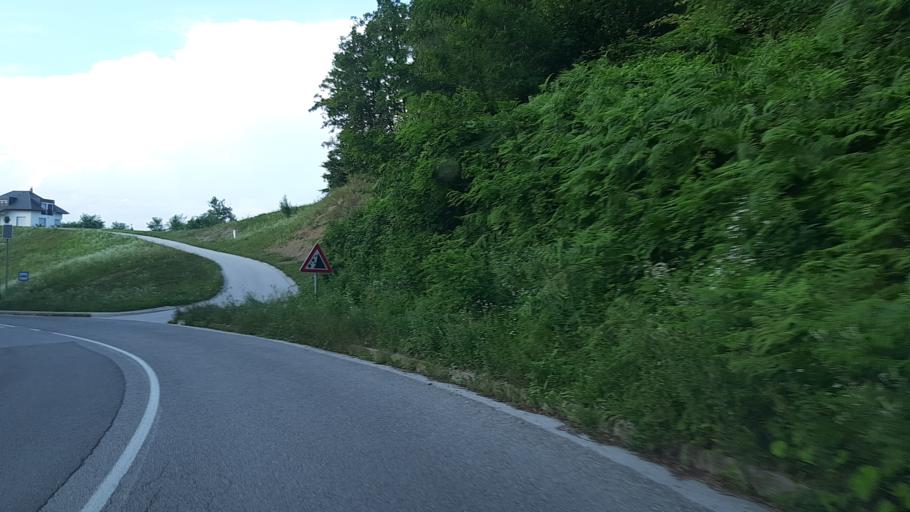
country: SI
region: Dobje
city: Dobje pri Planini
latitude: 46.1452
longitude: 15.4492
